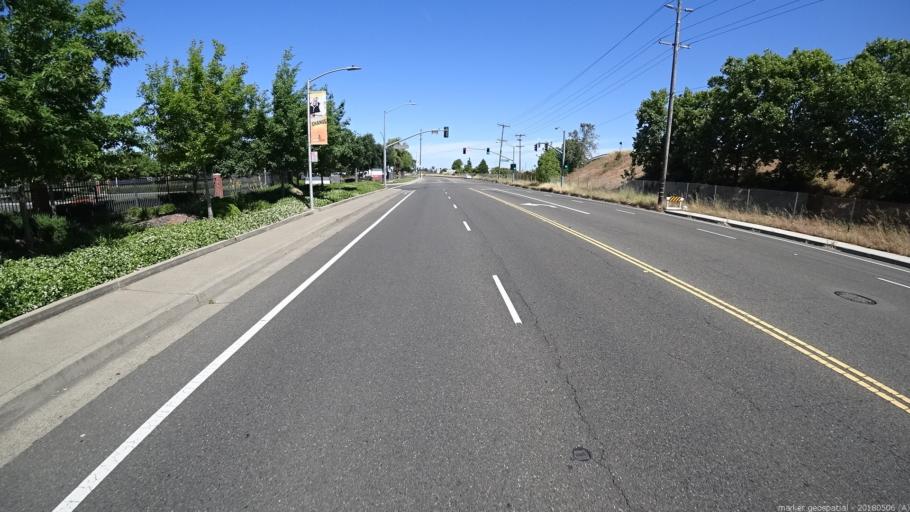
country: US
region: California
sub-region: Sacramento County
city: Florin
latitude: 38.4687
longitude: -121.4183
